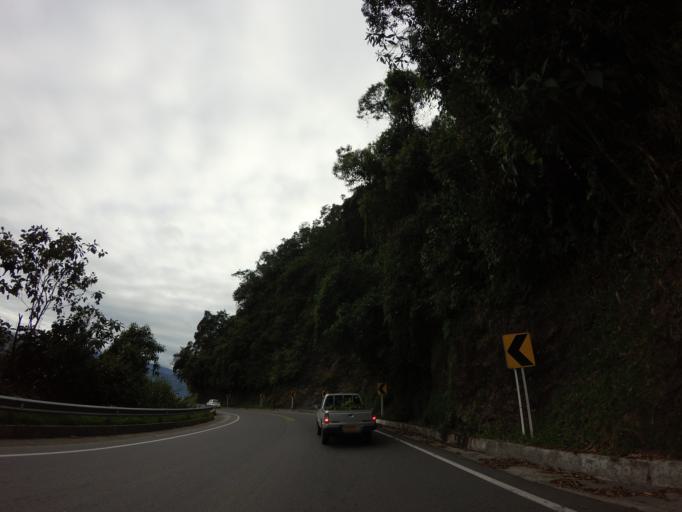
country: CO
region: Tolima
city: Herveo
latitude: 5.1095
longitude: -75.2207
